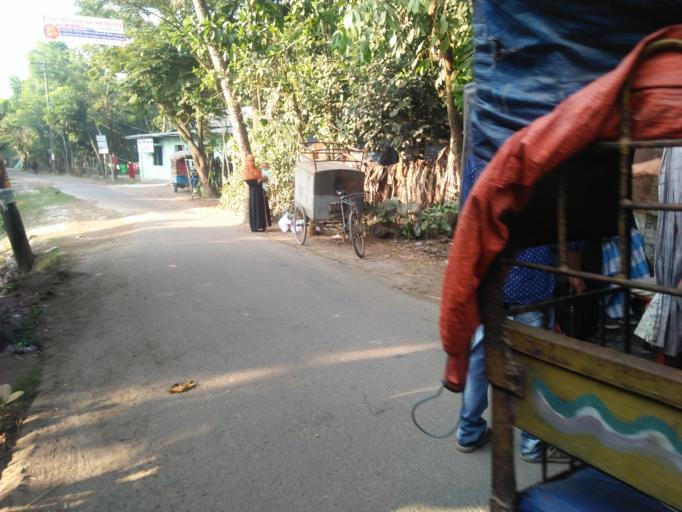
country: BD
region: Barisal
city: Bhola
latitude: 22.7510
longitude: 90.6350
